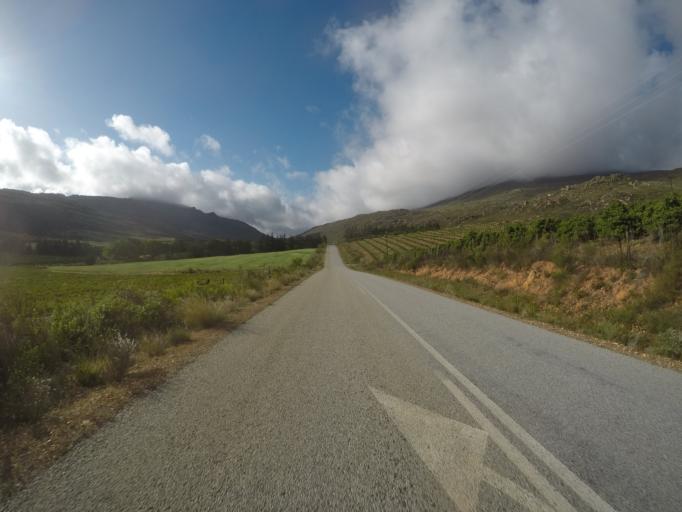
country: ZA
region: Western Cape
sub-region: West Coast District Municipality
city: Clanwilliam
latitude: -32.3566
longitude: 18.8517
